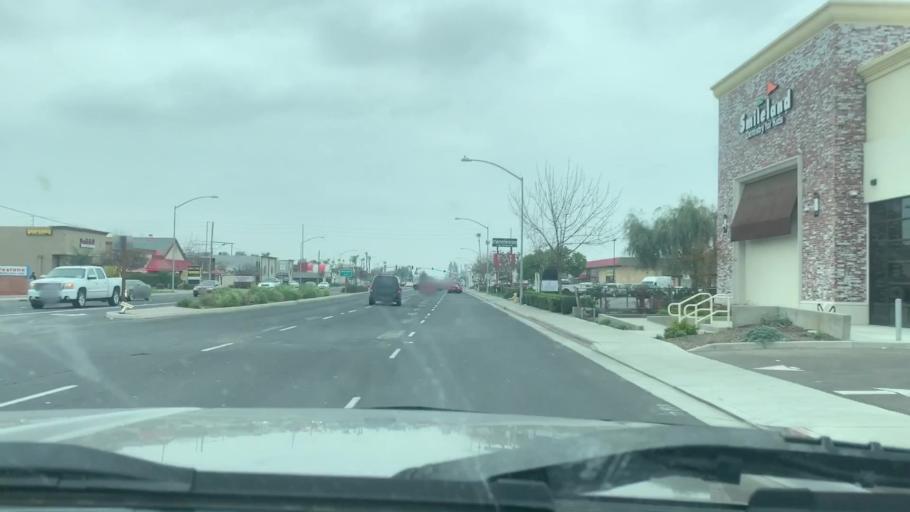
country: US
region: California
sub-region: Tulare County
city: Visalia
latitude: 36.3157
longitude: -119.3140
